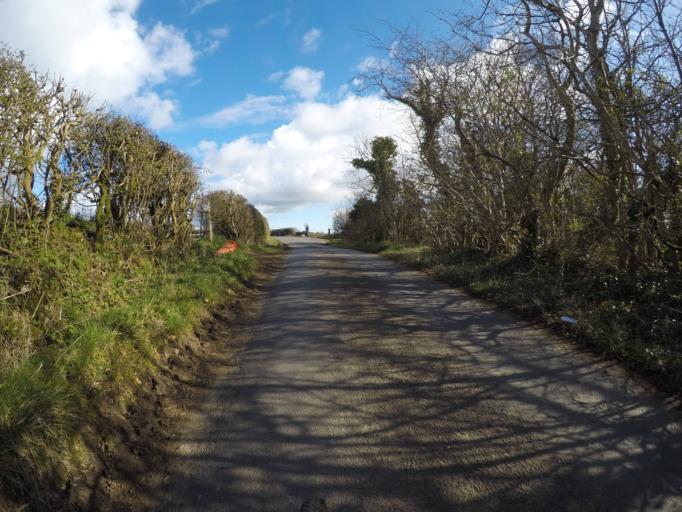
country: GB
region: Scotland
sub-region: North Ayrshire
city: Irvine
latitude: 55.6650
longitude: -4.6503
